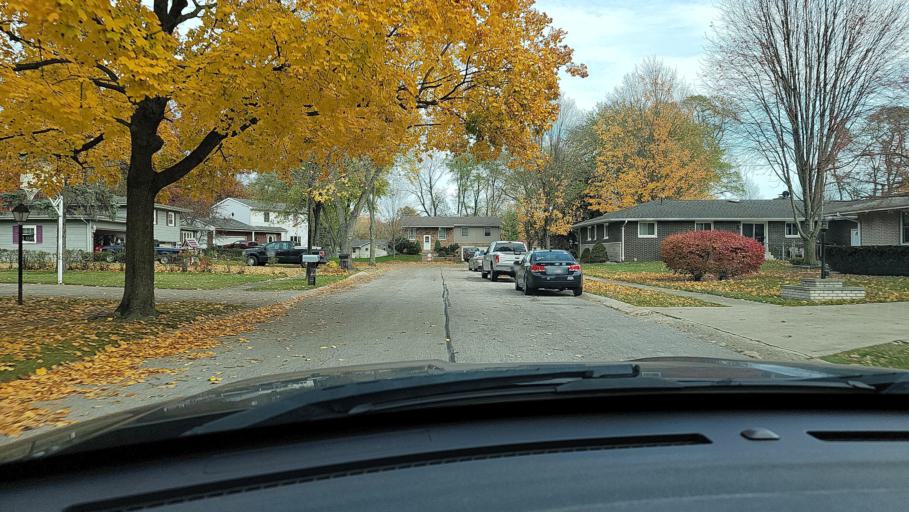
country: US
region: Indiana
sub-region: Porter County
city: Portage
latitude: 41.5973
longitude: -87.1576
